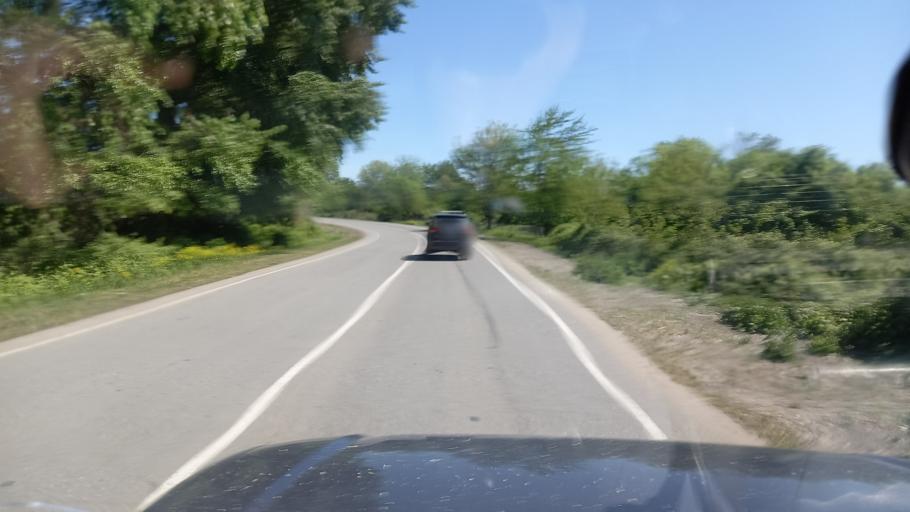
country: RU
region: Dagestan
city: Samur
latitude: 41.7391
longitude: 48.4813
